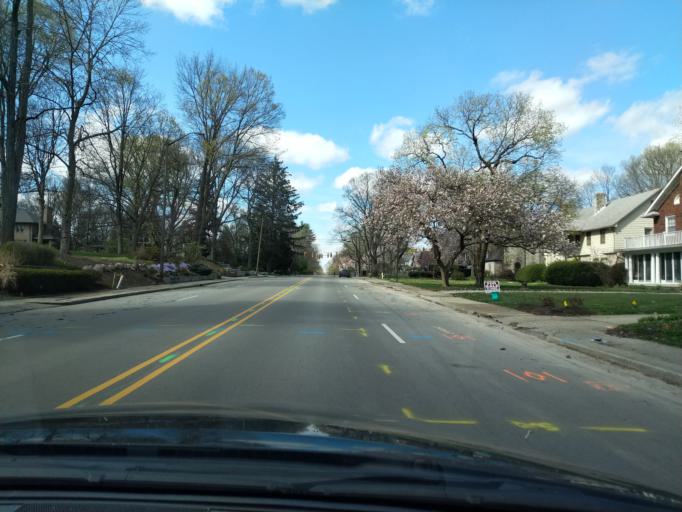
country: US
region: Indiana
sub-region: Marion County
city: Broad Ripple
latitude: 39.8530
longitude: -86.1501
